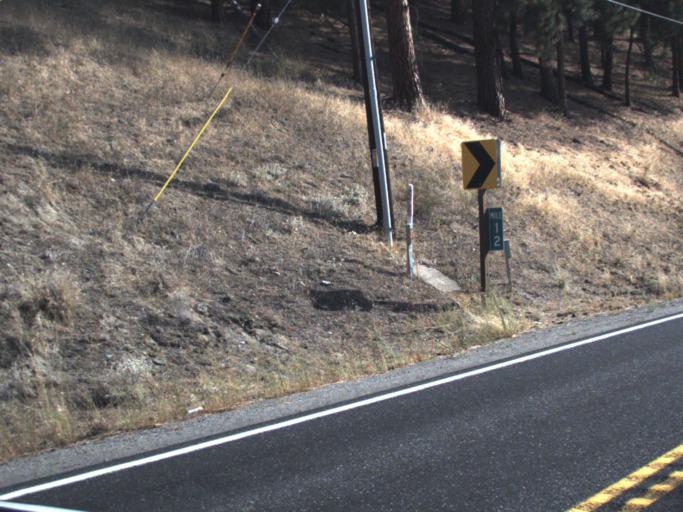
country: US
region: Washington
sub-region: Spokane County
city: Fairwood
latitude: 47.8035
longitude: -117.5488
